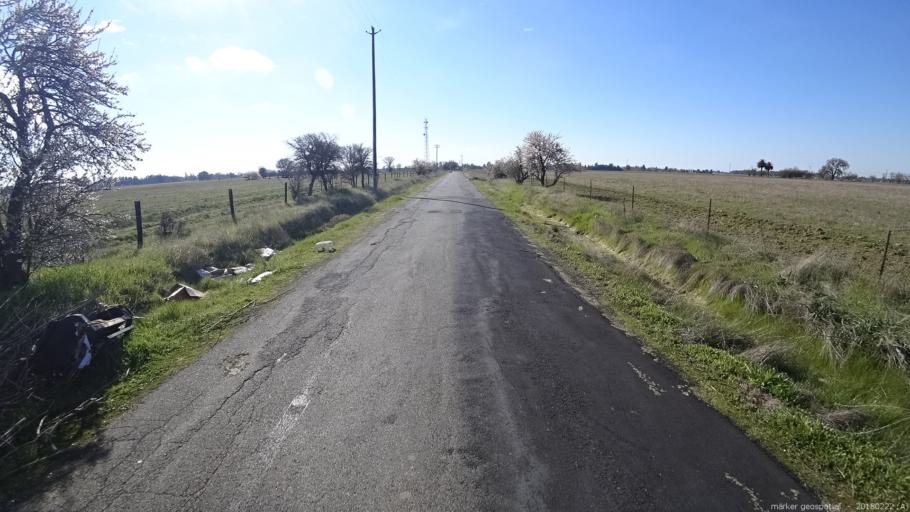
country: US
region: California
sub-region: Sacramento County
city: Elverta
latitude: 38.7312
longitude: -121.4110
